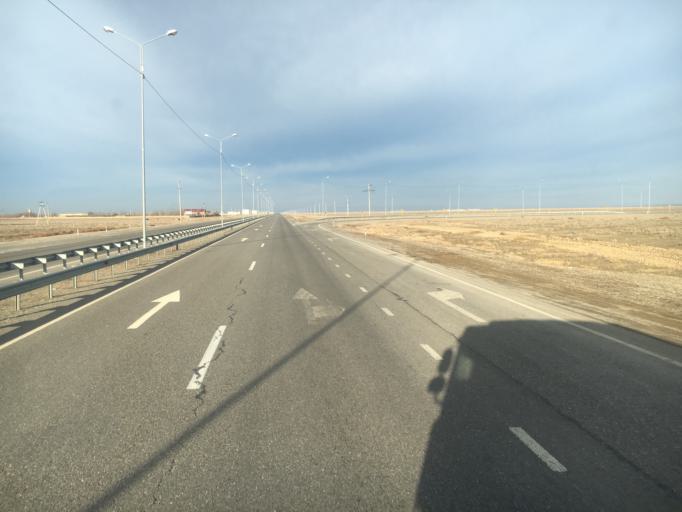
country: KZ
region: Ongtustik Qazaqstan
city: Turkestan
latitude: 43.4150
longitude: 68.0246
